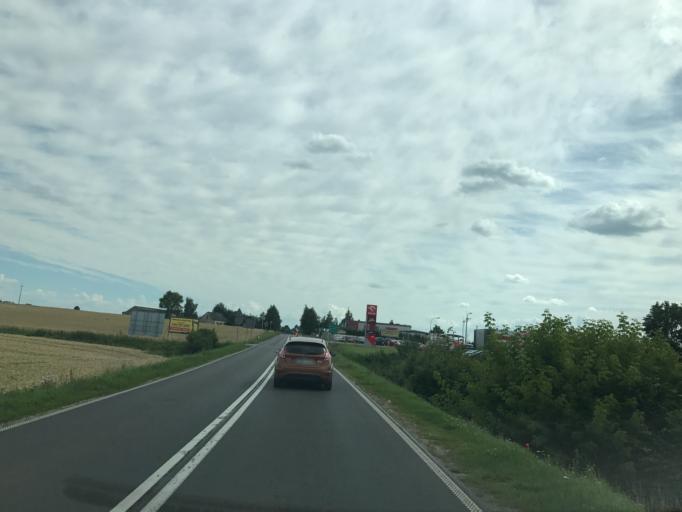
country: PL
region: Kujawsko-Pomorskie
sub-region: Powiat brodnicki
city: Brodnica
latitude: 53.2229
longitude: 19.3854
